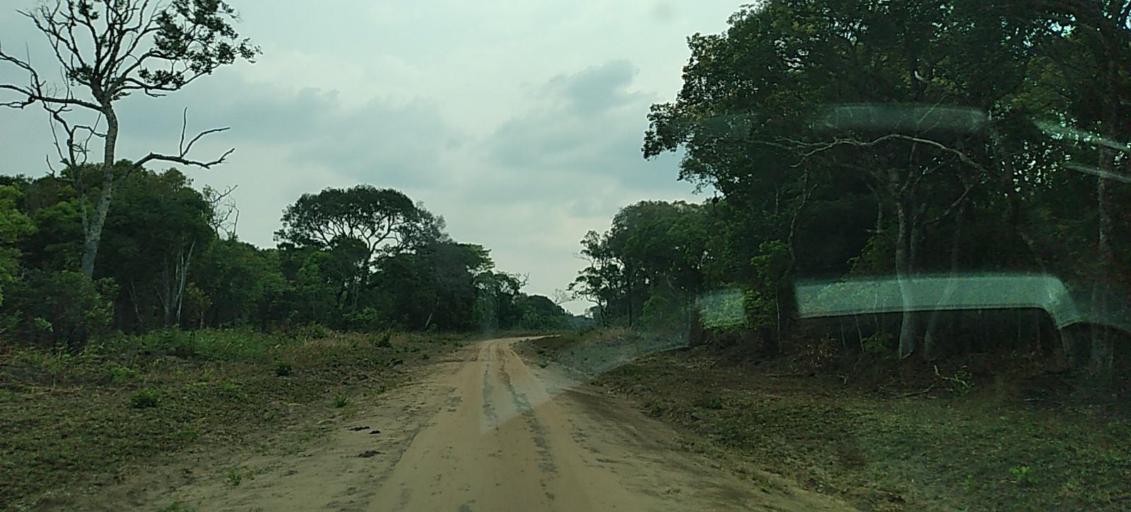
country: ZM
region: North-Western
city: Mwinilunga
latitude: -11.4117
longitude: 24.6171
